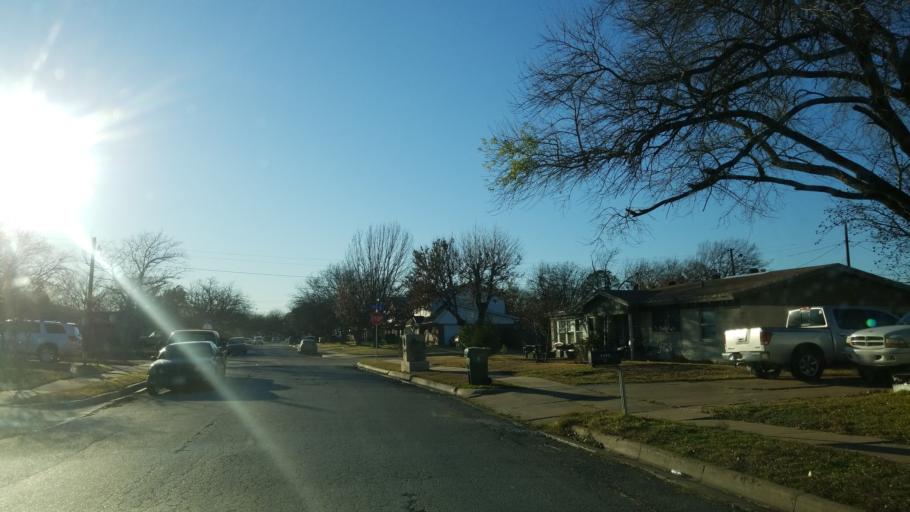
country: US
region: Texas
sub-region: Tarrant County
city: Arlington
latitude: 32.7249
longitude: -97.0664
